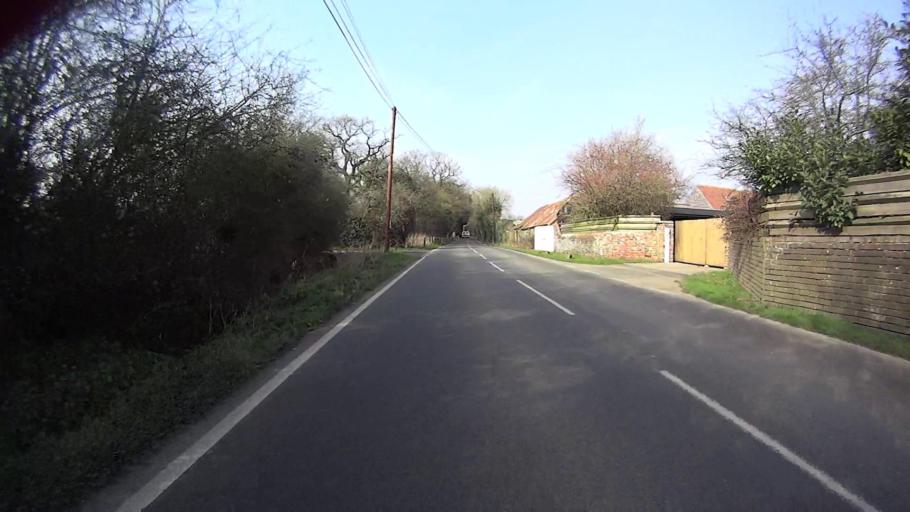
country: GB
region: England
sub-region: West Sussex
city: Copthorne
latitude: 51.1797
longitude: -0.0878
